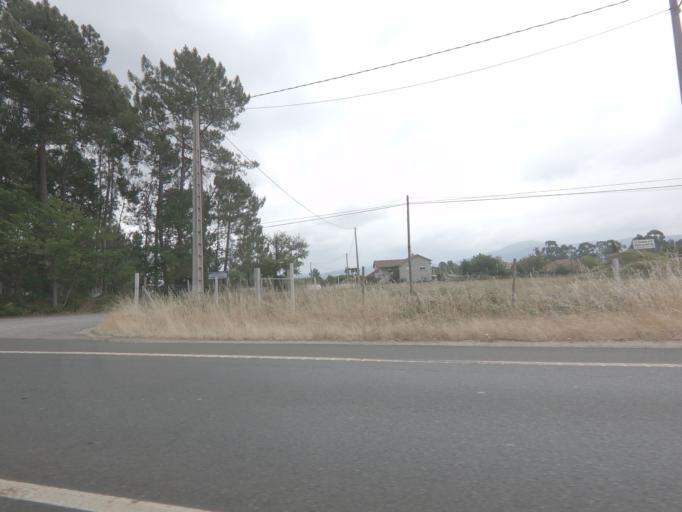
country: ES
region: Galicia
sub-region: Provincia de Pontevedra
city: Tomino
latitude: 41.9937
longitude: -8.6993
